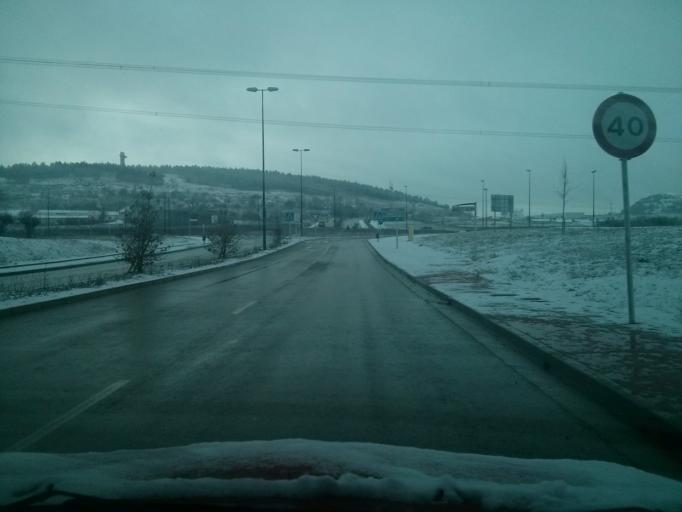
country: ES
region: Castille and Leon
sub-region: Provincia de Burgos
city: Burgos
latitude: 42.3674
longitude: -3.6962
